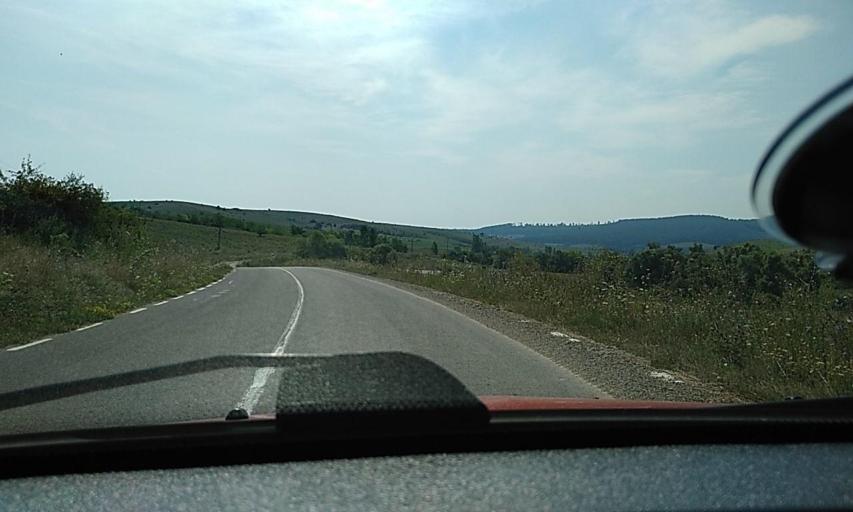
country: RO
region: Brasov
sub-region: Oras Rupea
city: Fiser
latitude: 46.0303
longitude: 25.1419
